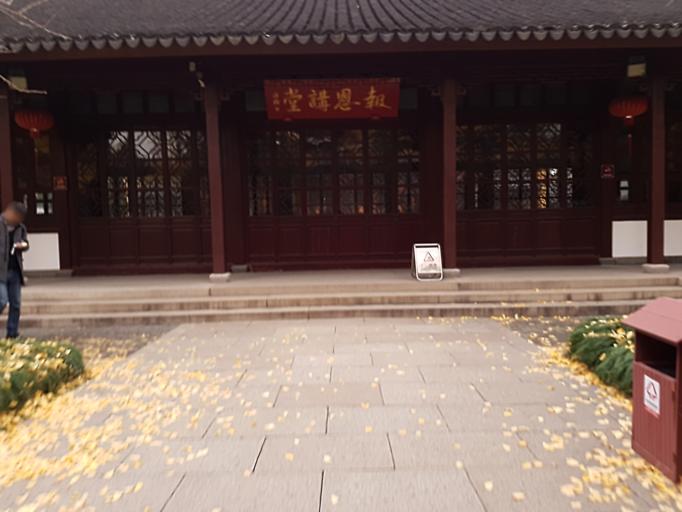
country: CN
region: Jiangsu Sheng
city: Pingjianglu
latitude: 31.3248
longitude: 120.6153
